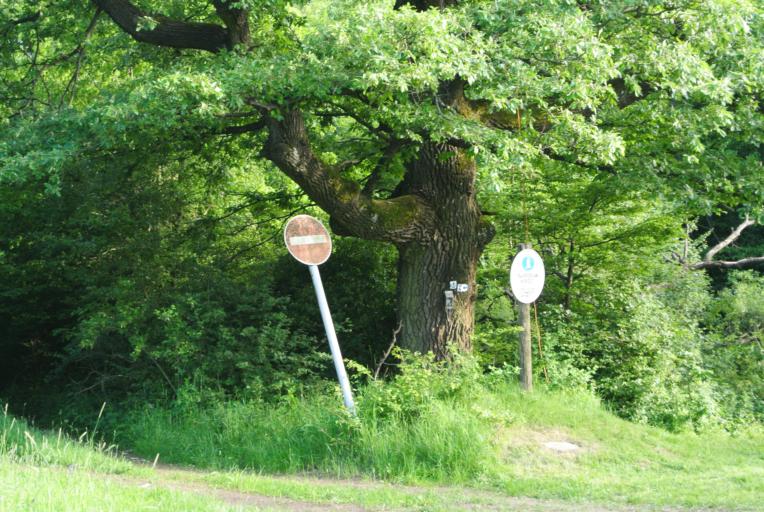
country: HU
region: Komarom-Esztergom
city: Tardos
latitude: 47.6610
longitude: 18.4766
